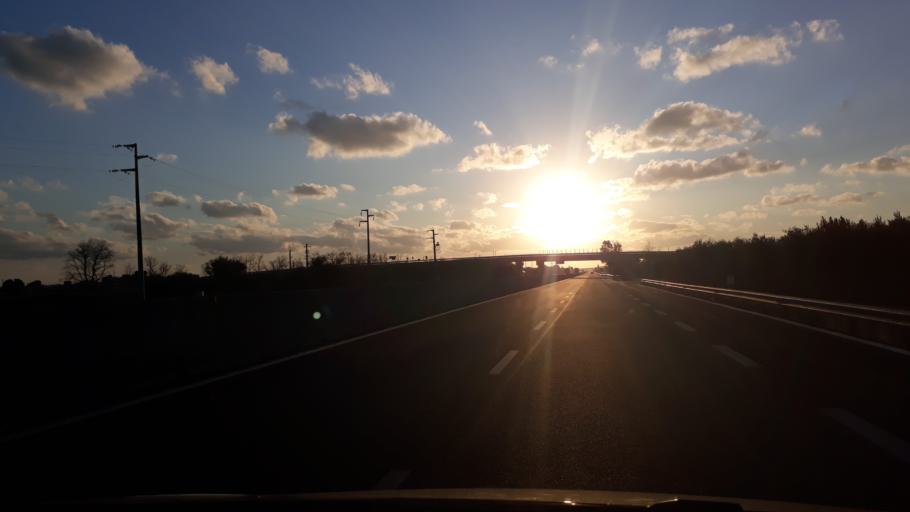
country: IT
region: Apulia
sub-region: Provincia di Brindisi
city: Carovigno
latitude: 40.7423
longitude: 17.7149
